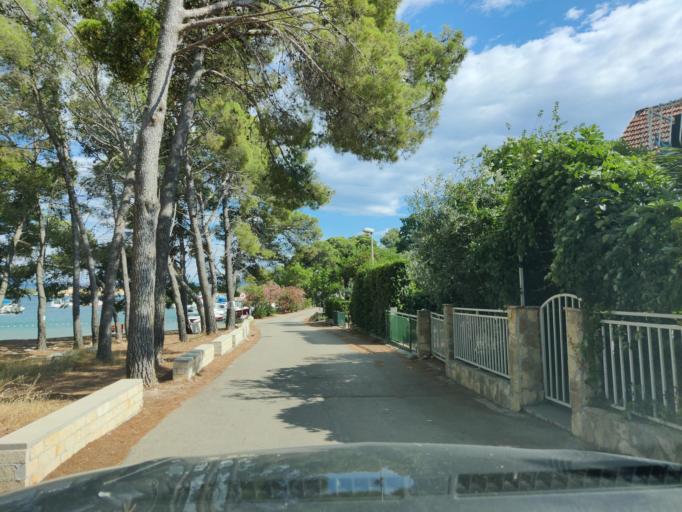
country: HR
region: Sibensko-Kniniska
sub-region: Grad Sibenik
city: Sibenik
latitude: 43.7263
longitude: 15.8469
